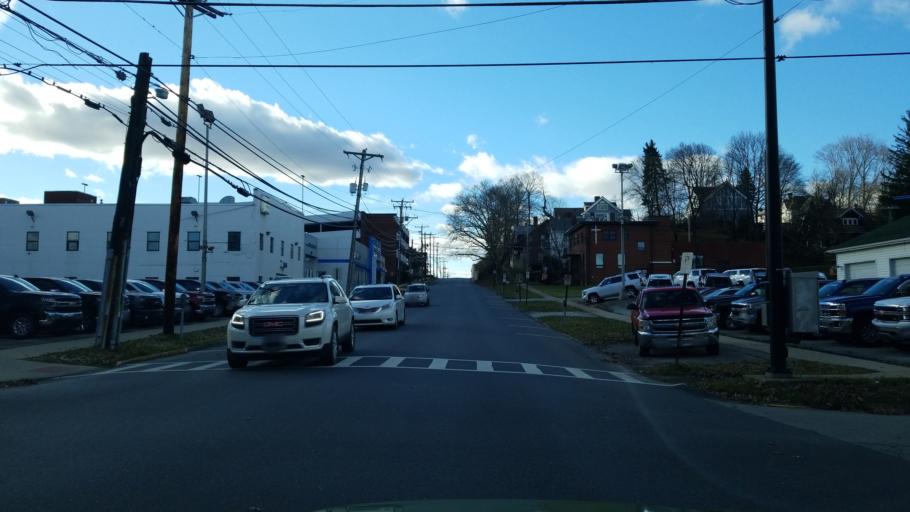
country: US
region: Pennsylvania
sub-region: Indiana County
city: Indiana
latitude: 40.6243
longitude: -79.1507
